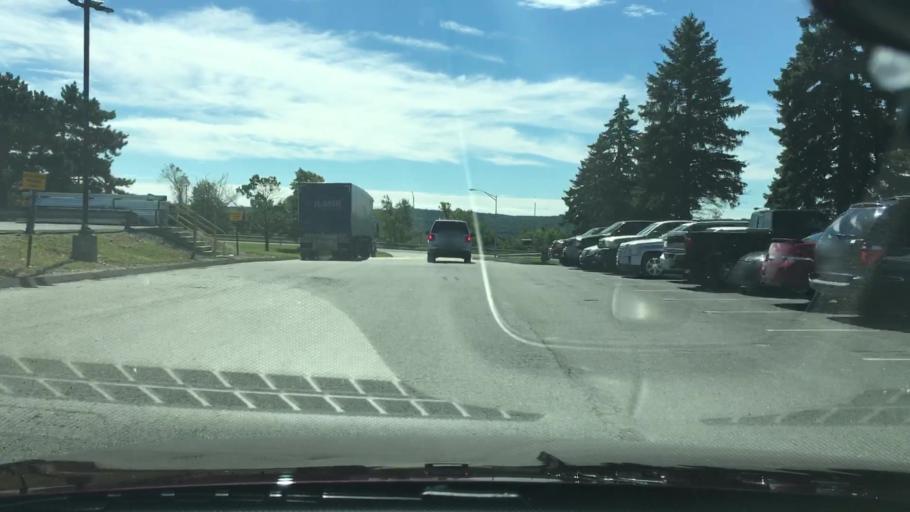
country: US
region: Connecticut
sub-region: Litchfield County
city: Terryville
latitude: 41.6935
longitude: -72.9818
